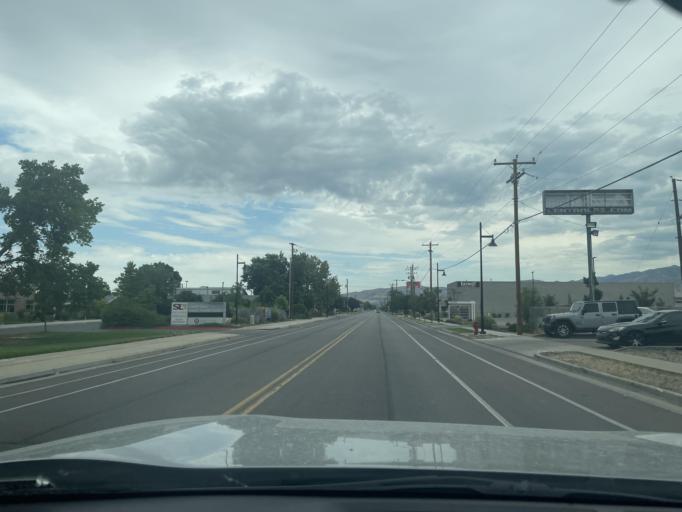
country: US
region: Utah
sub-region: Salt Lake County
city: Centerfield
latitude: 40.6900
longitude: -111.8911
